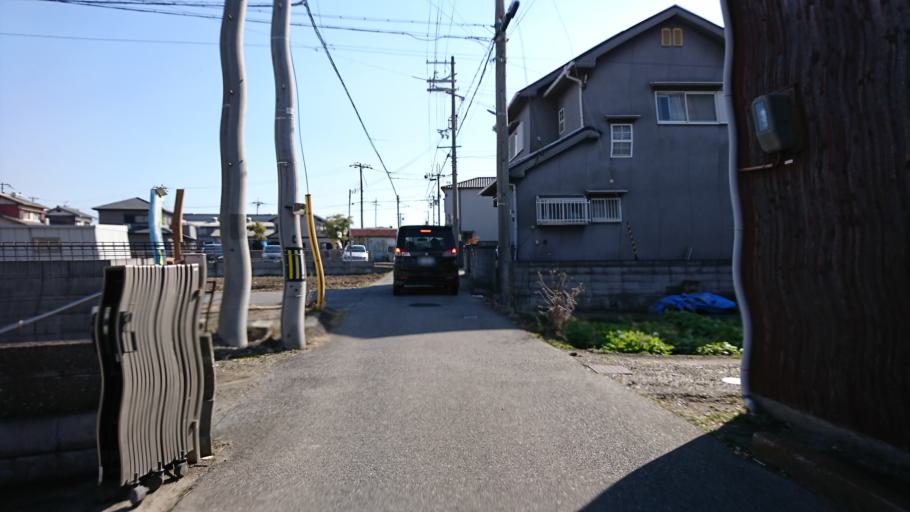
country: JP
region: Hyogo
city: Kakogawacho-honmachi
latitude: 34.7292
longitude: 134.8622
